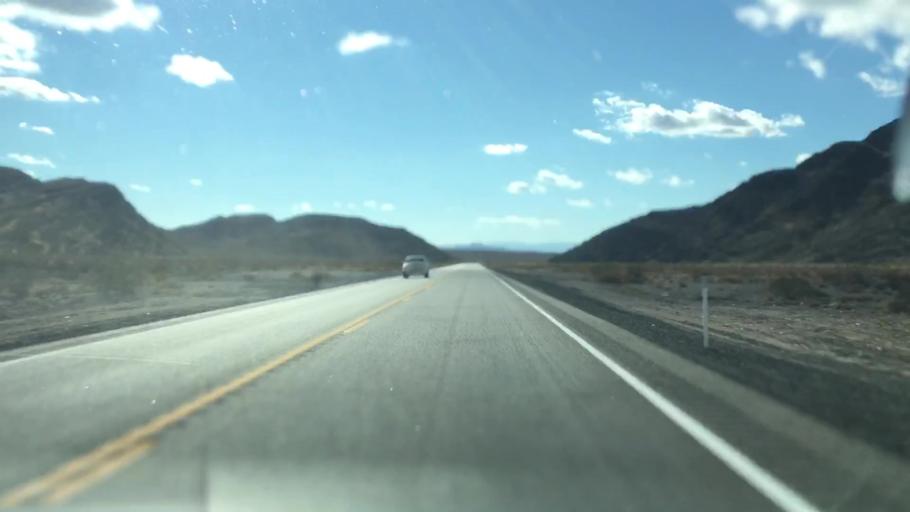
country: US
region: Nevada
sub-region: Nye County
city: Pahrump
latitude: 36.5735
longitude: -116.0747
